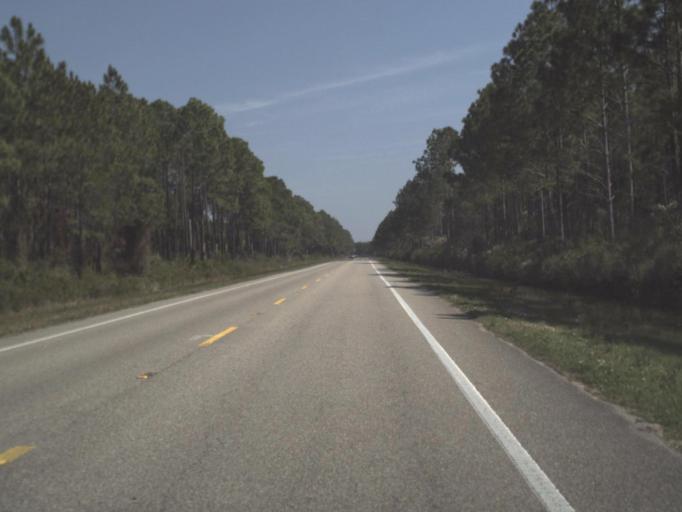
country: US
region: Florida
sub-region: Franklin County
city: Apalachicola
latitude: 29.7252
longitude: -85.1233
